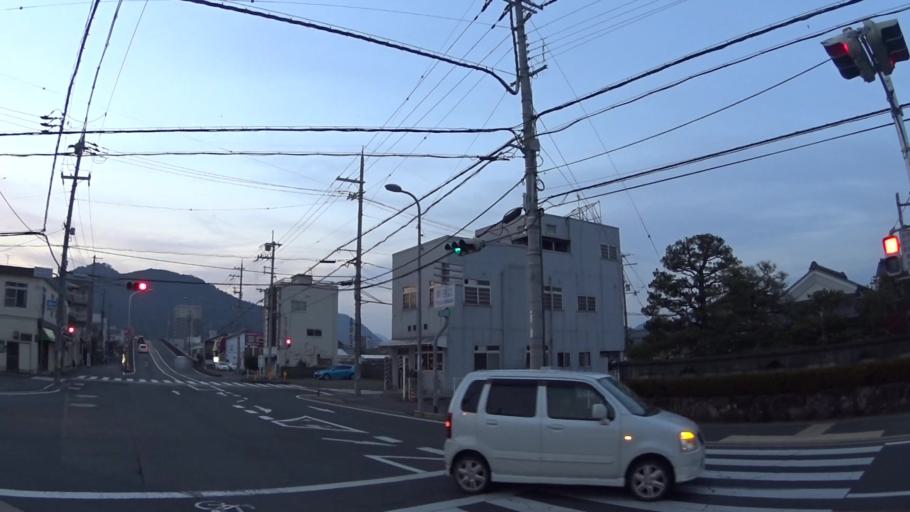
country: JP
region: Kyoto
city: Maizuru
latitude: 35.4451
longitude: 135.3333
